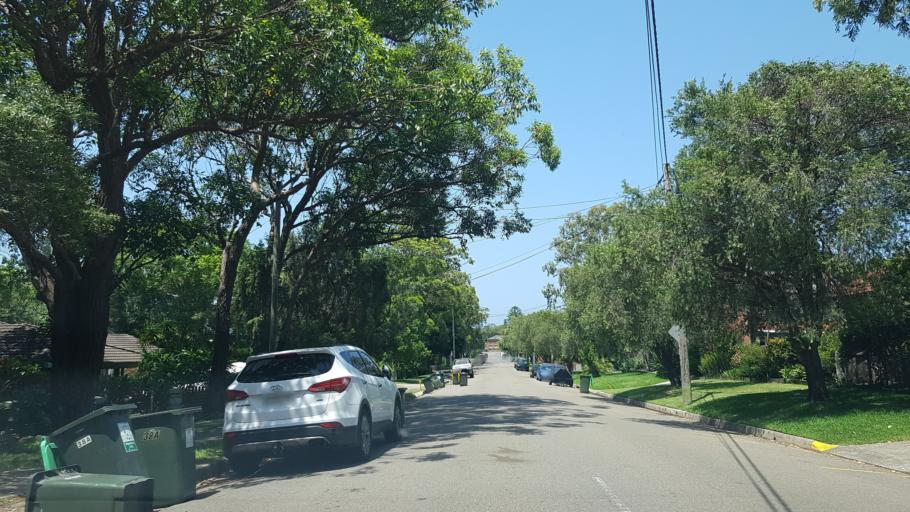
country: AU
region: New South Wales
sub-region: Pittwater
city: Newport
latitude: -33.6583
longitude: 151.3129
